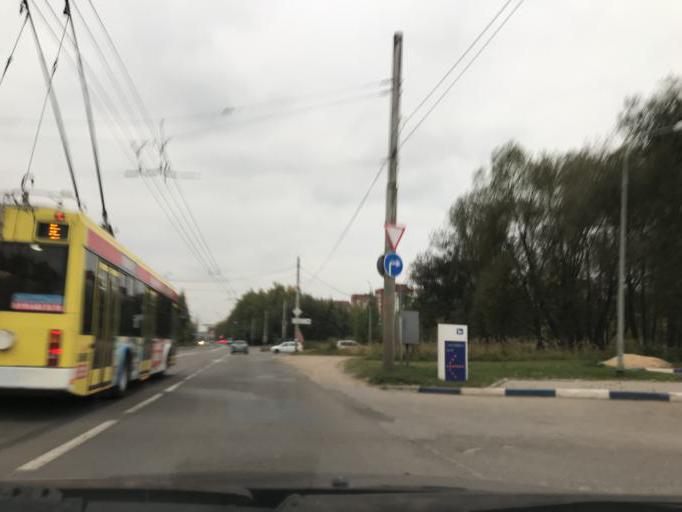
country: RU
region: Kaluga
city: Kaluga
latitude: 54.5948
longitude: 36.2583
